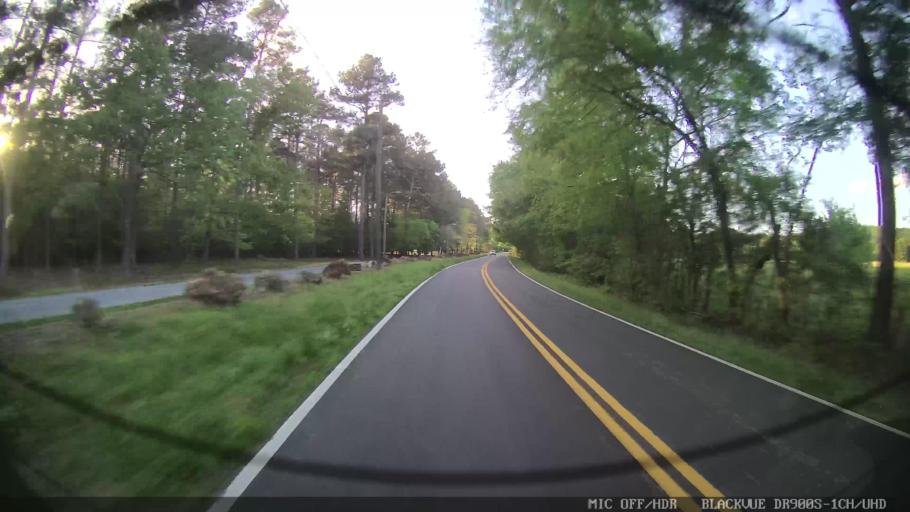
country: US
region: Georgia
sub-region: Bartow County
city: Cartersville
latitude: 34.1363
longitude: -84.8086
